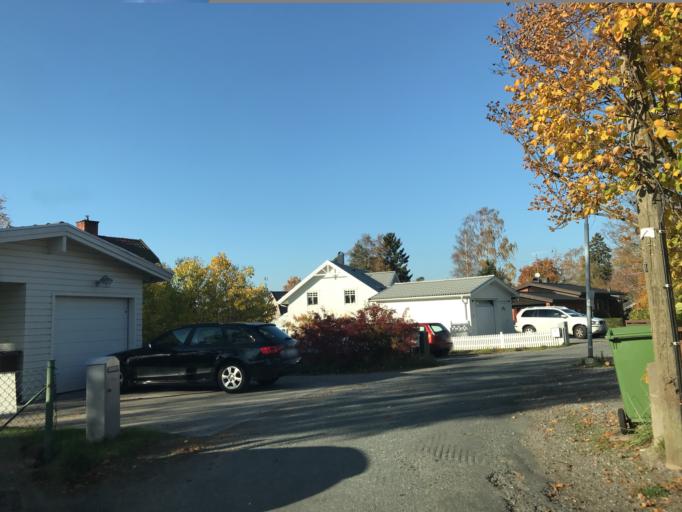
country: SE
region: Stockholm
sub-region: Sollentuna Kommun
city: Sollentuna
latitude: 59.4219
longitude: 17.9350
